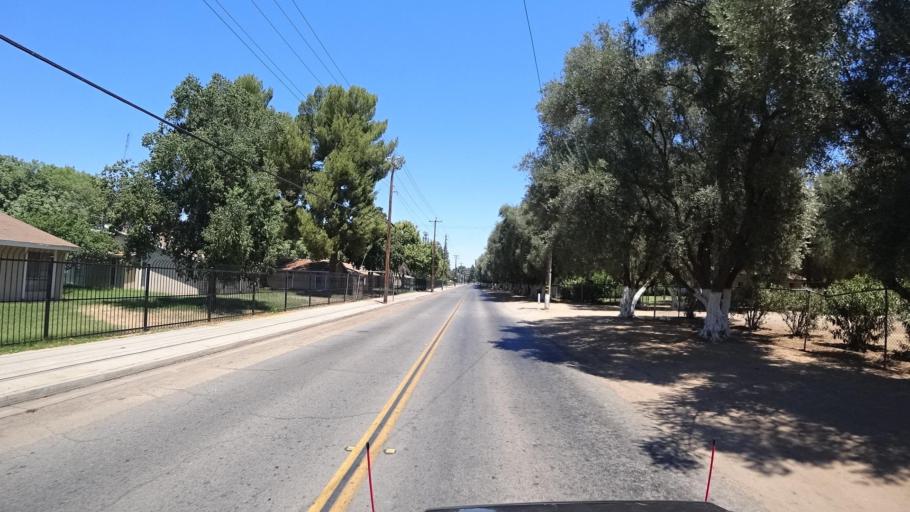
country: US
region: California
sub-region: Fresno County
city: Sunnyside
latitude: 36.7226
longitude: -119.7275
